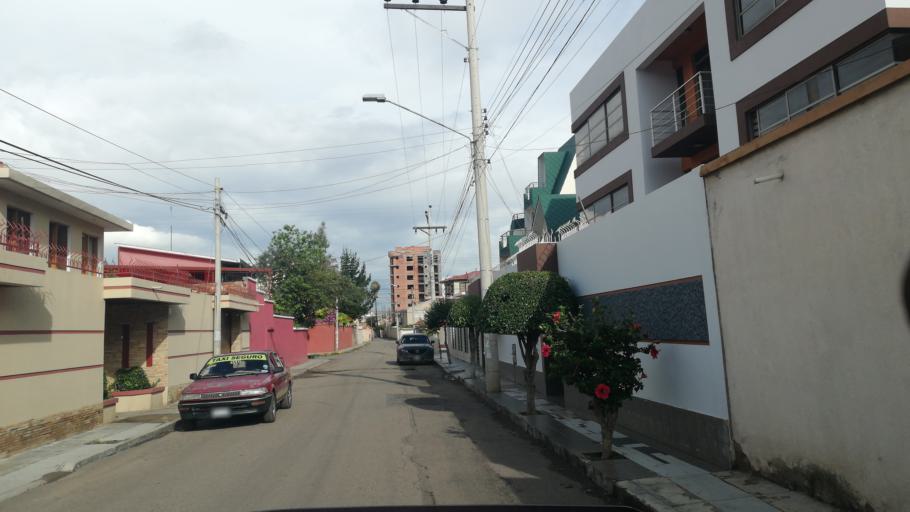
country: BO
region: Cochabamba
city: Cochabamba
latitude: -17.3750
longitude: -66.1778
